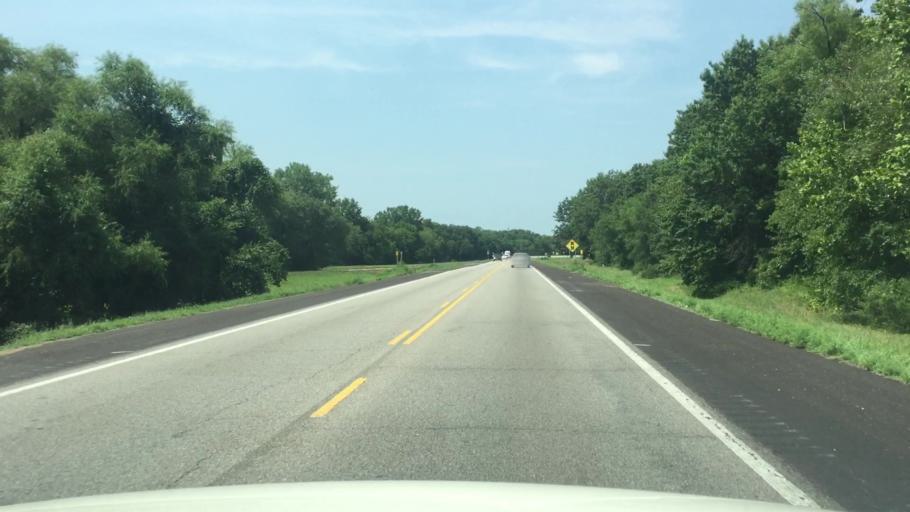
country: US
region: Kansas
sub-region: Crawford County
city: Pittsburg
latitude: 37.4031
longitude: -94.7225
